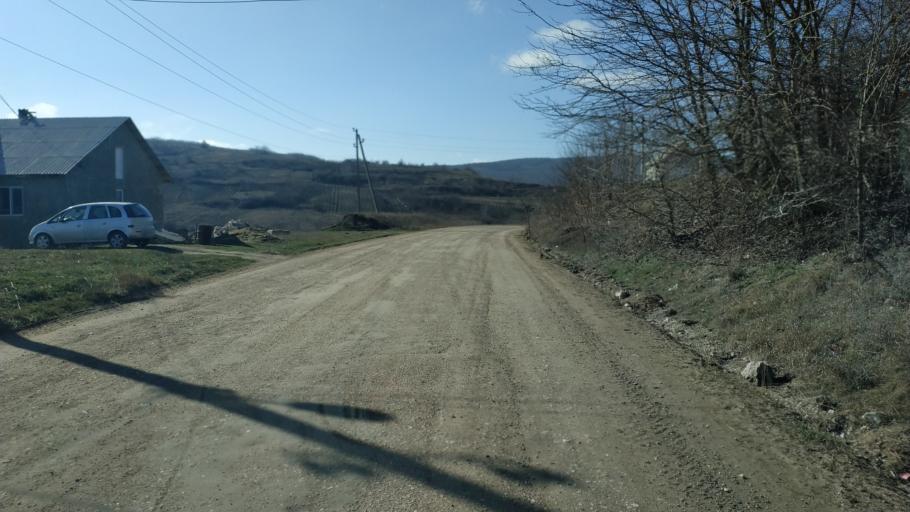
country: MD
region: Hincesti
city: Hincesti
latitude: 46.9303
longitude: 28.6345
